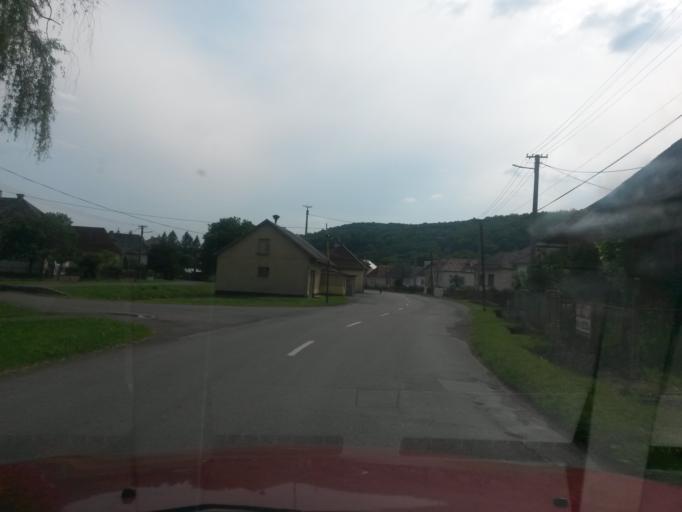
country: SK
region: Presovsky
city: Humenne
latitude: 48.9923
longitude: 22.0107
